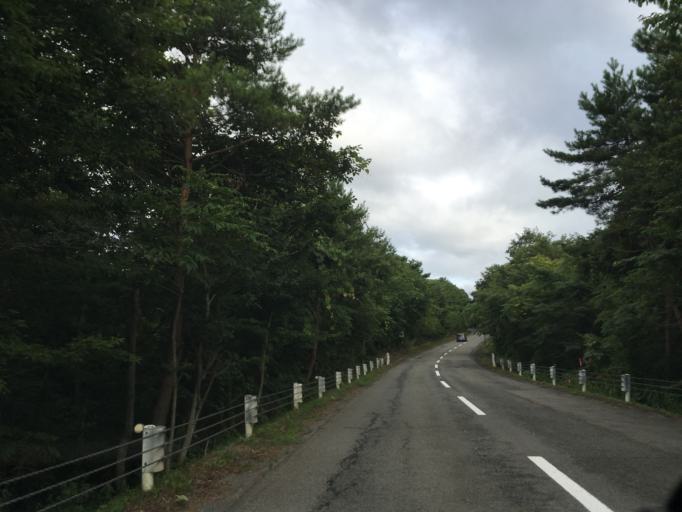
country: JP
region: Fukushima
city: Inawashiro
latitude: 37.6084
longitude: 140.2305
